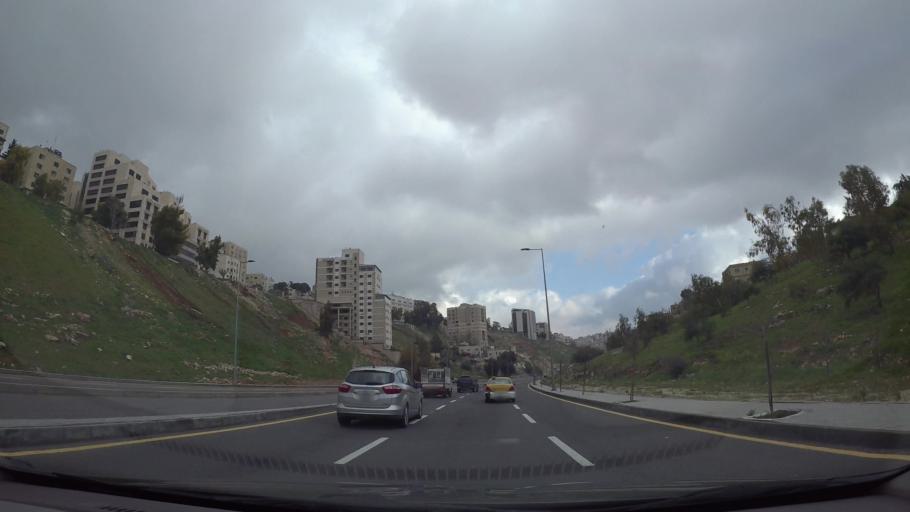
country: JO
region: Amman
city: Amman
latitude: 31.9511
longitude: 35.9000
